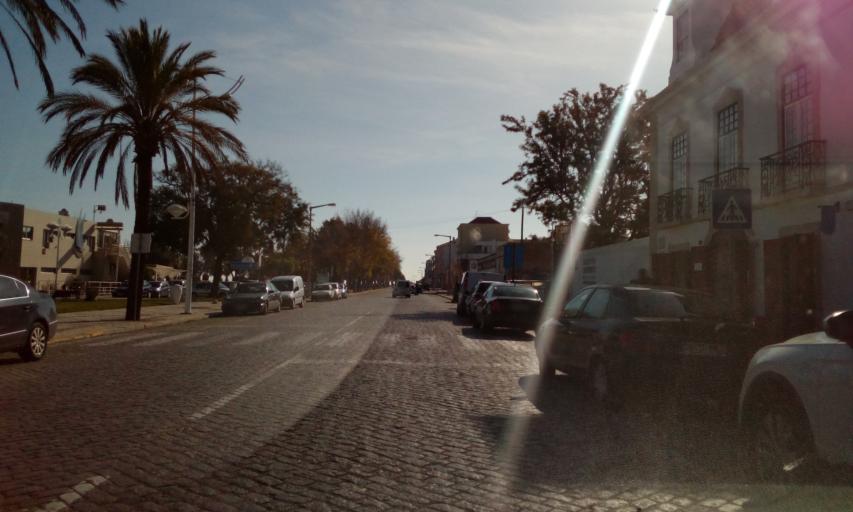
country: PT
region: Faro
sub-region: Vila Real de Santo Antonio
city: Vila Real de Santo Antonio
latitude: 37.1934
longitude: -7.4140
